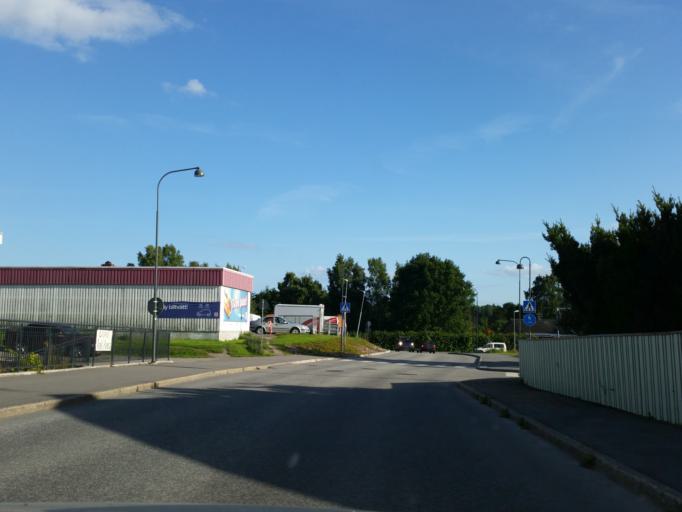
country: SE
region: Soedermanland
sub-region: Trosa Kommun
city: Vagnharad
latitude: 58.9455
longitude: 17.4871
